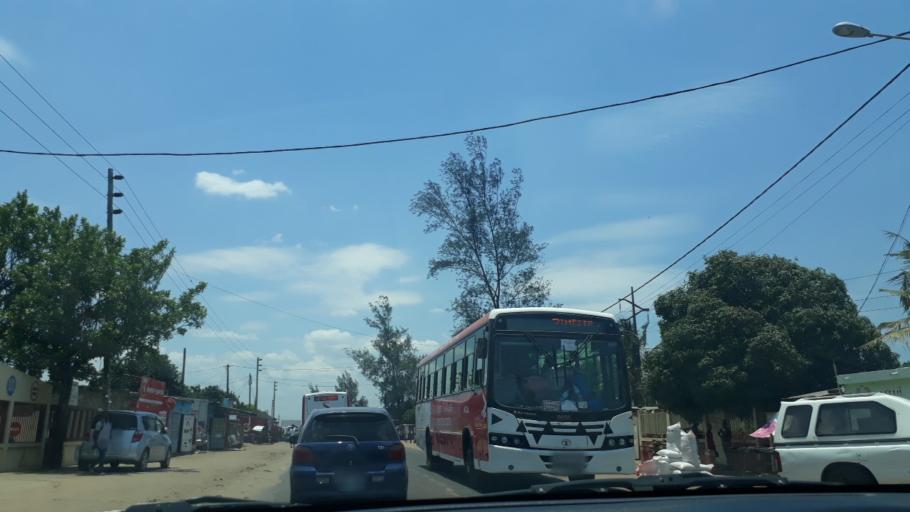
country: MZ
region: Maputo City
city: Maputo
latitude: -25.8905
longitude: 32.6030
